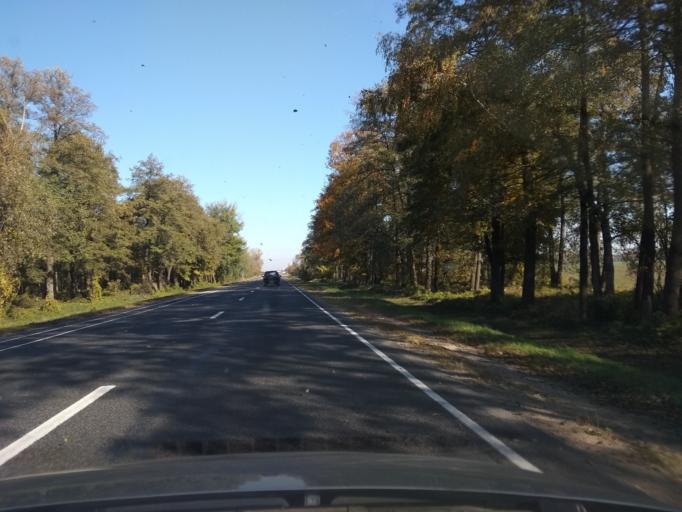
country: BY
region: Brest
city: Kobryn
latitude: 52.1685
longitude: 24.3167
